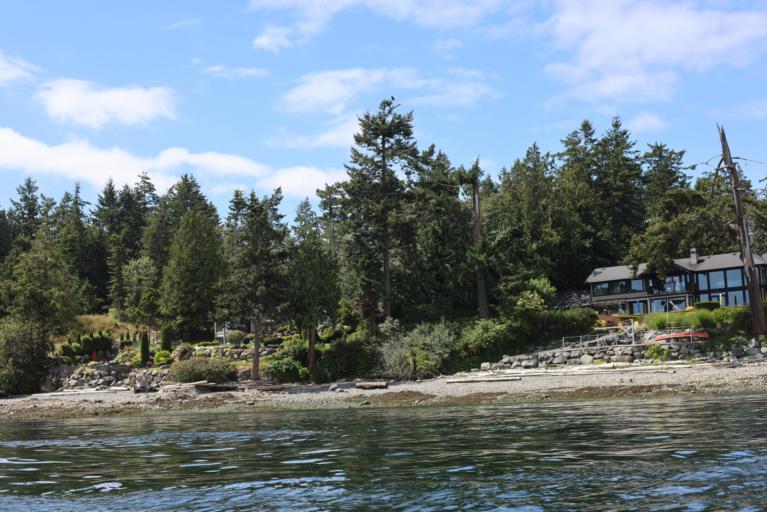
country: CA
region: British Columbia
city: North Saanich
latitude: 48.6091
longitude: -123.3941
